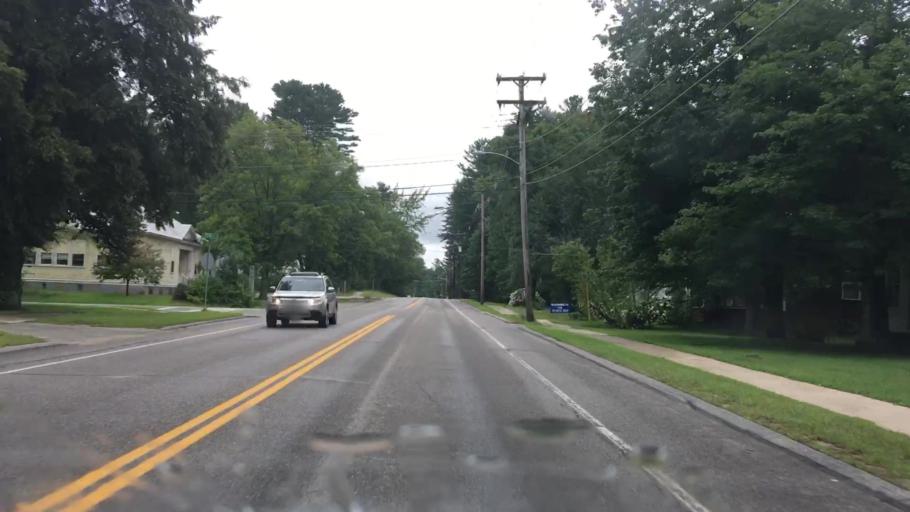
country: US
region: Maine
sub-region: Oxford County
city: Fryeburg
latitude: 44.0148
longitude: -70.9761
